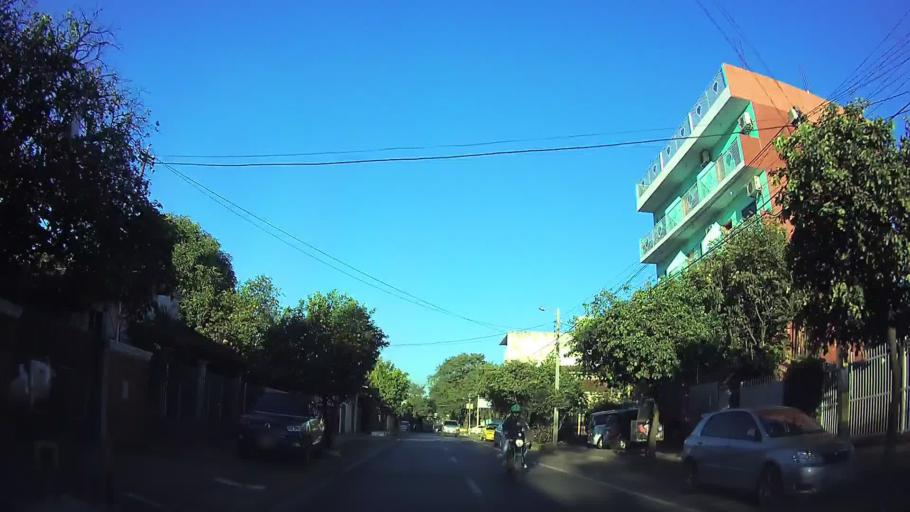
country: PY
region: Central
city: San Lorenzo
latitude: -25.2675
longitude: -57.4977
